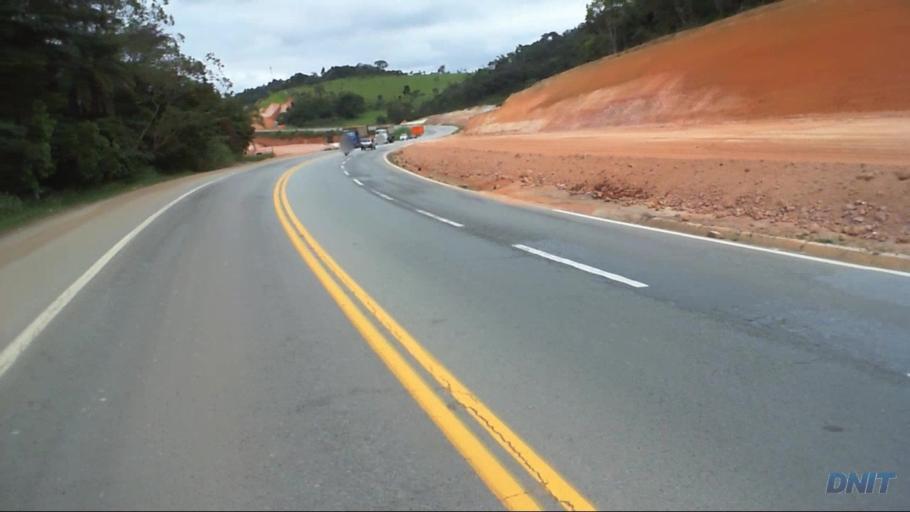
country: BR
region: Minas Gerais
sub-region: Caete
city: Caete
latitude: -19.7443
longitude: -43.5497
